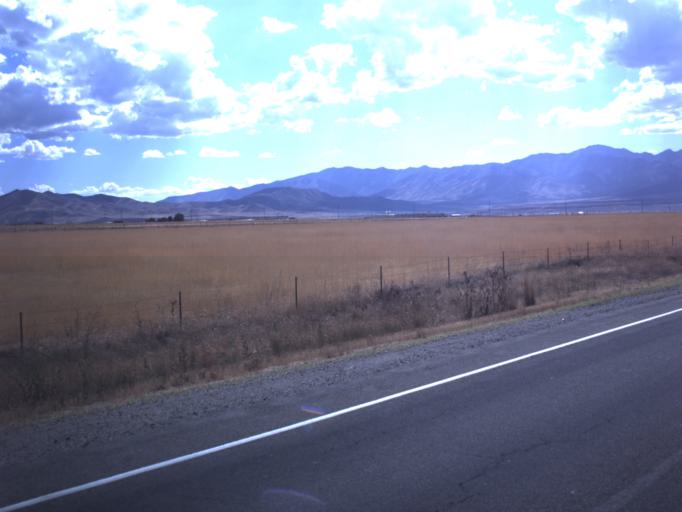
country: US
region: Utah
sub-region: Tooele County
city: Tooele
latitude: 40.5508
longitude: -112.3286
